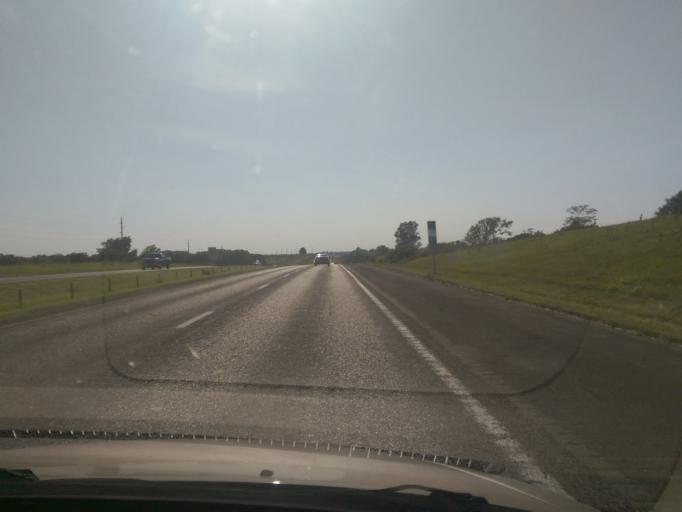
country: US
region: Missouri
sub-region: Lafayette County
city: Higginsville
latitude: 38.9927
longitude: -93.6931
